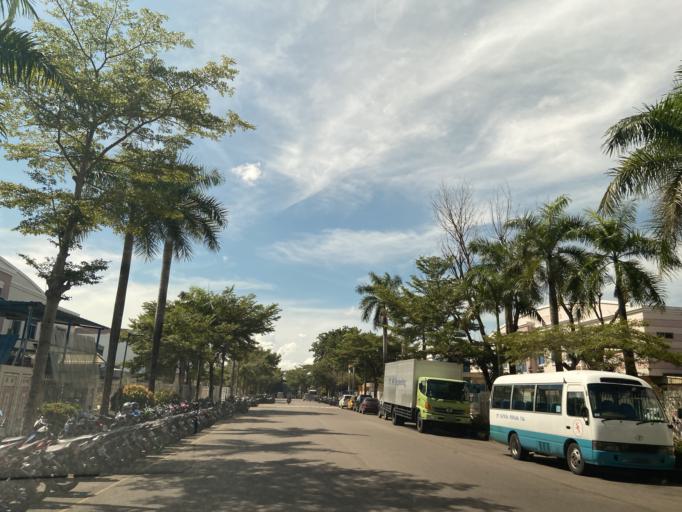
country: SG
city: Singapore
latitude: 1.1087
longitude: 104.0636
